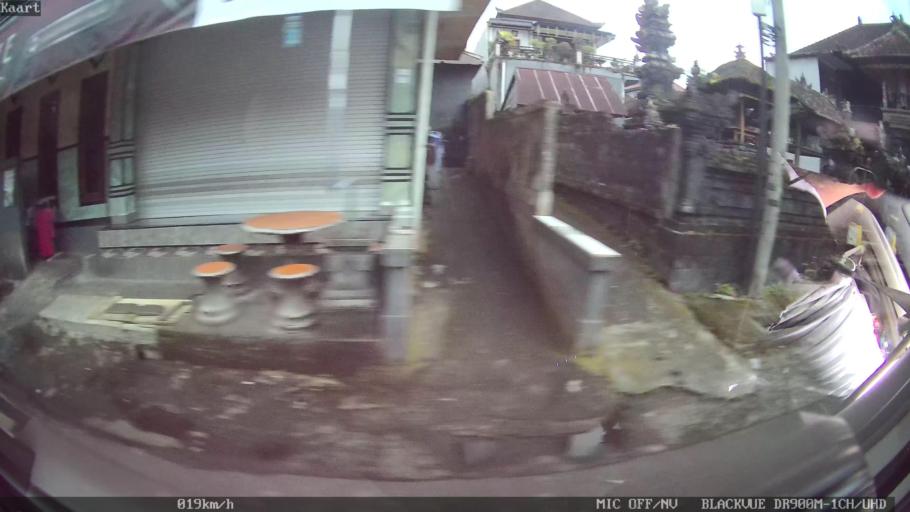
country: ID
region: Bali
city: Peneng
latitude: -8.3507
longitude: 115.2059
